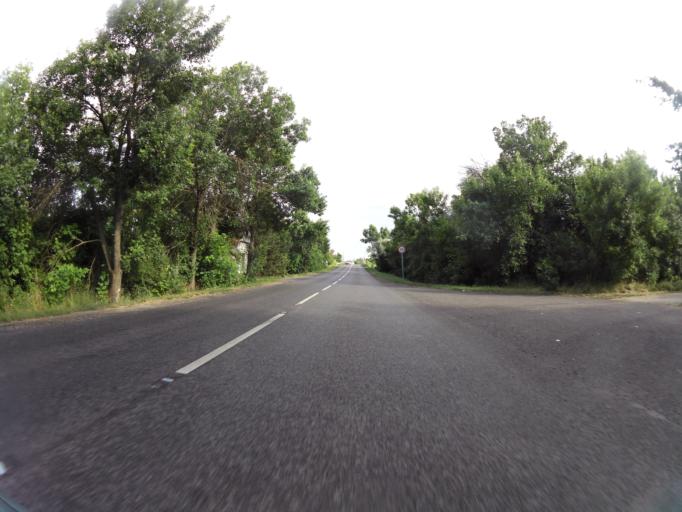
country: HU
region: Csongrad
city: Szeged
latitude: 46.2851
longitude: 20.1419
